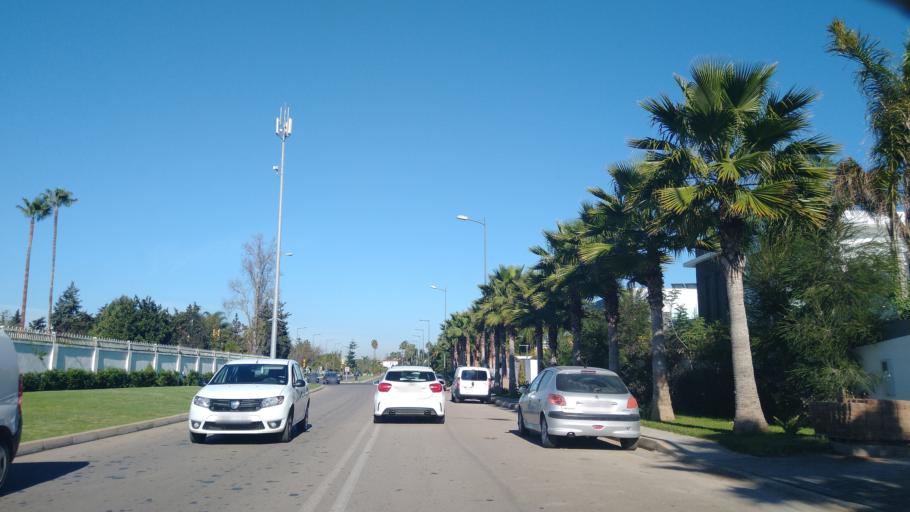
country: MA
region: Rabat-Sale-Zemmour-Zaer
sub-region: Rabat
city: Rabat
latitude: 33.9587
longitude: -6.8419
